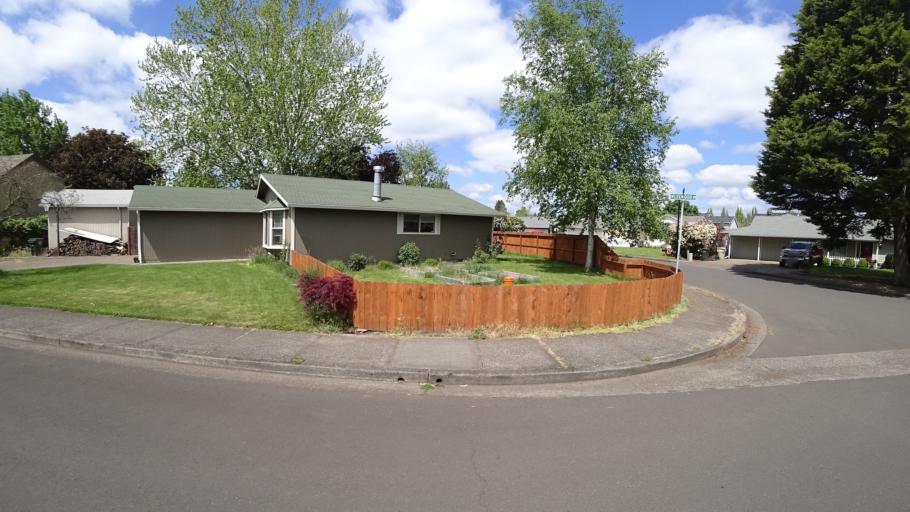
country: US
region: Oregon
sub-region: Washington County
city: Aloha
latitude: 45.5058
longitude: -122.8893
